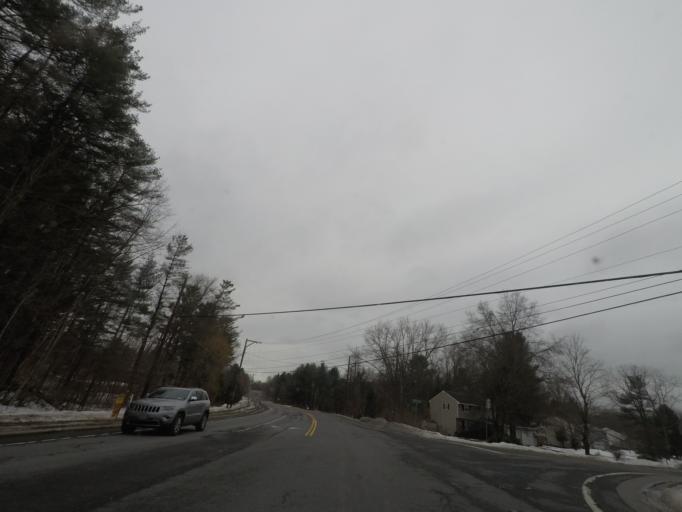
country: US
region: New York
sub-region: Albany County
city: Westmere
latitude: 42.6895
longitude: -73.9004
